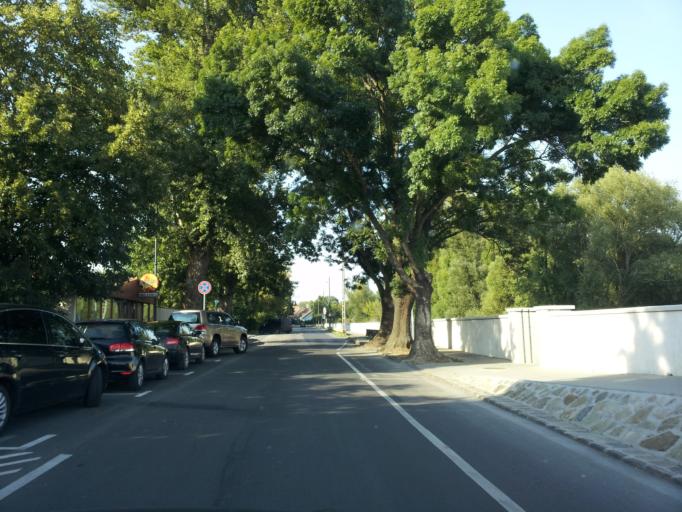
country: HU
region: Pest
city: Szentendre
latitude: 47.6706
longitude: 19.0788
